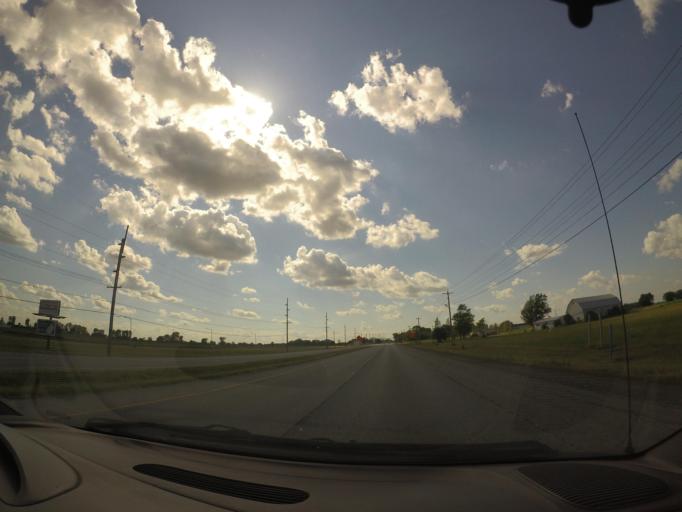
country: US
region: Ohio
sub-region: Sandusky County
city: Clyde
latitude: 41.3156
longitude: -82.9958
